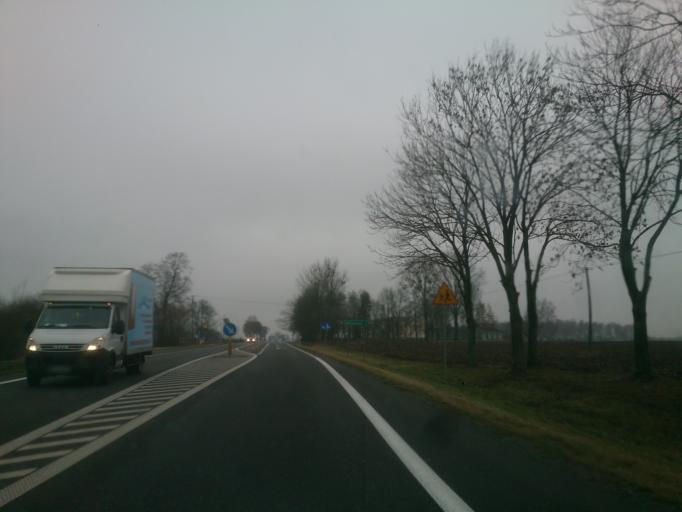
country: PL
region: Masovian Voivodeship
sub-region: Powiat plocki
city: Drobin
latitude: 52.6923
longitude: 20.0487
